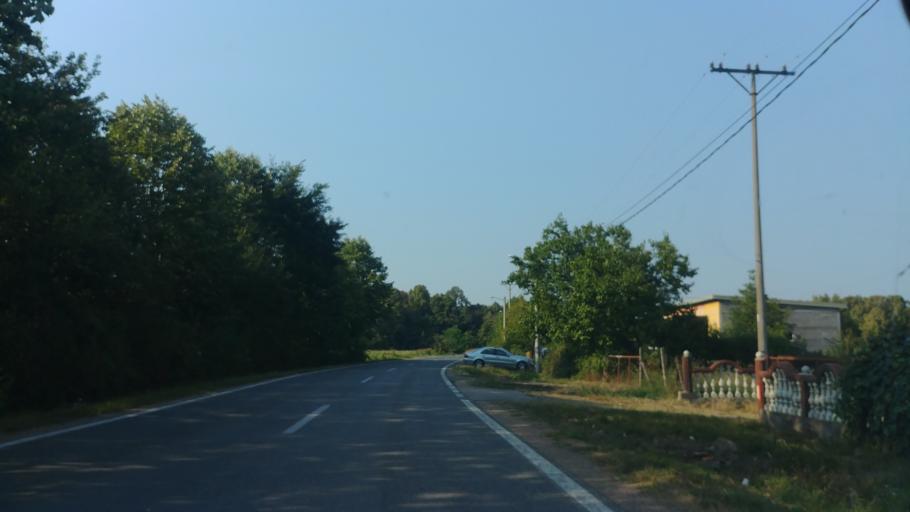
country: BA
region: Brcko
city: Brcko
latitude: 44.7913
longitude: 18.8162
